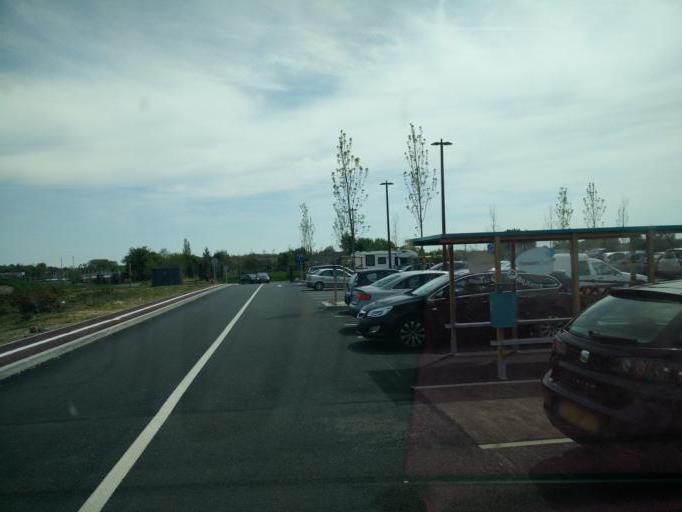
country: FR
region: Brittany
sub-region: Departement d'Ille-et-Vilaine
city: Dinard
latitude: 48.6113
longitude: -2.0621
